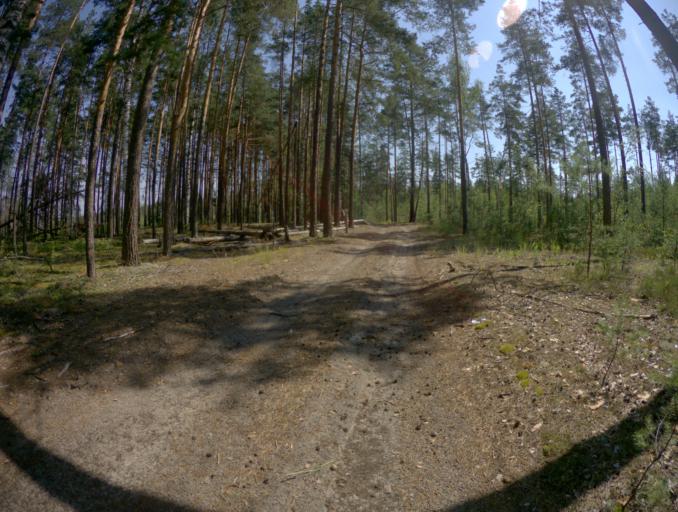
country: RU
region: Ivanovo
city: Talitsy
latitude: 56.4093
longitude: 42.2682
